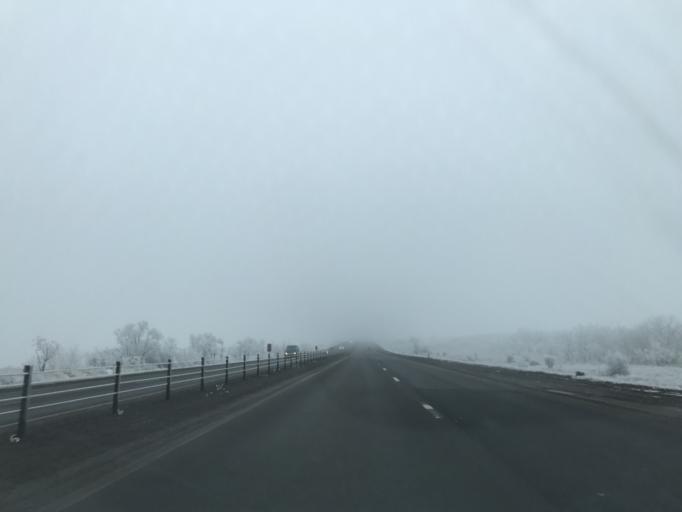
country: RU
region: Rostov
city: Likhoy
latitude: 48.1546
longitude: 40.2615
